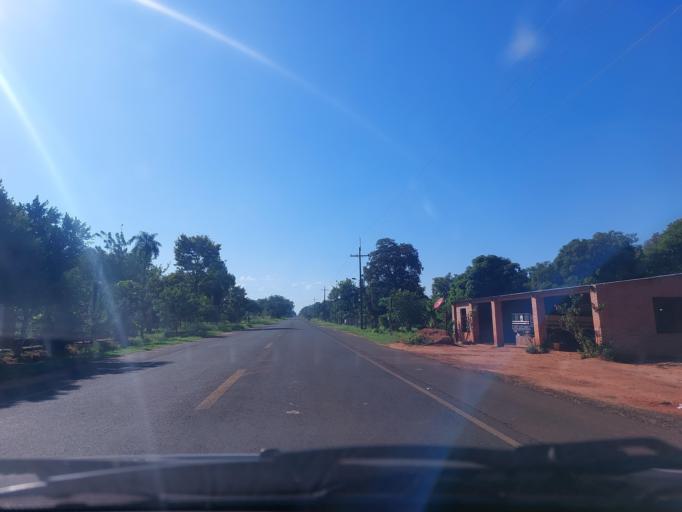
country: PY
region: San Pedro
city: Guayaybi
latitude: -24.5320
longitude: -56.4972
